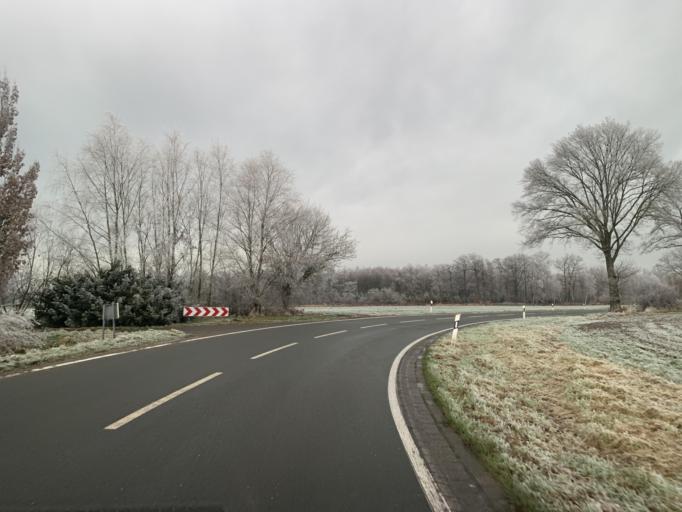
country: DE
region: North Rhine-Westphalia
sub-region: Regierungsbezirk Munster
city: Greven
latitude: 52.0478
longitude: 7.5427
